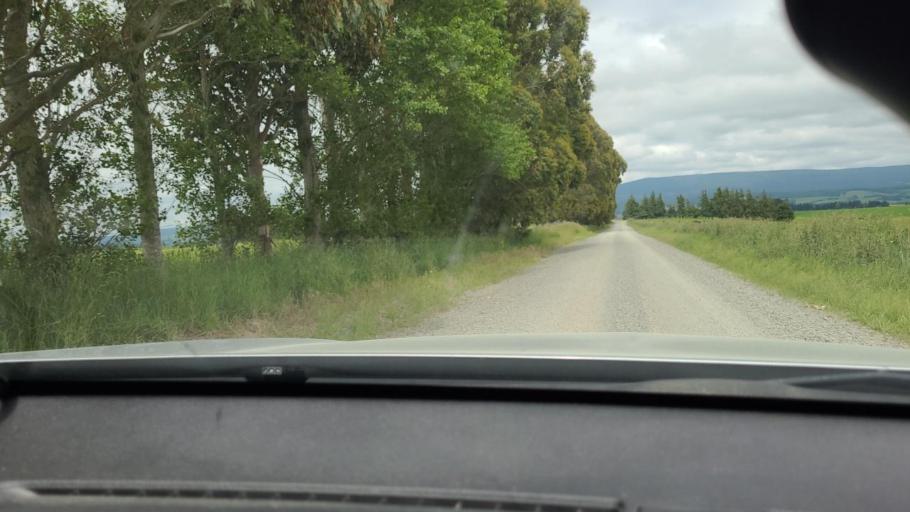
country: NZ
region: Southland
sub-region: Southland District
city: Riverton
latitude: -46.0644
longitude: 167.9854
